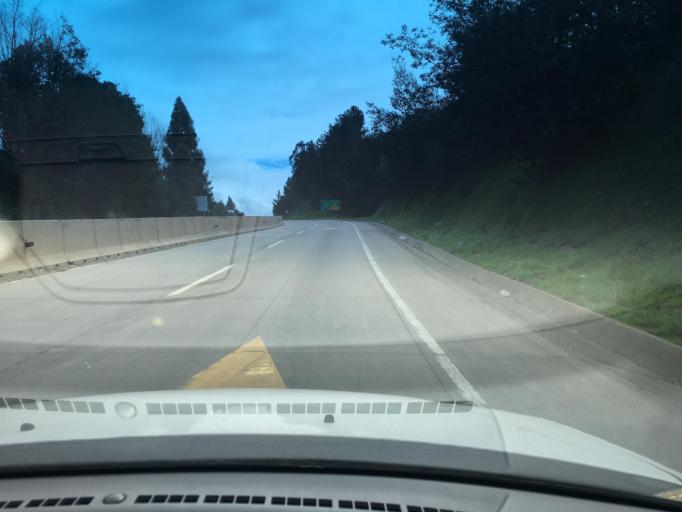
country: CL
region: Valparaiso
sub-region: Provincia de Valparaiso
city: Vina del Mar
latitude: -33.1070
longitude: -71.5654
